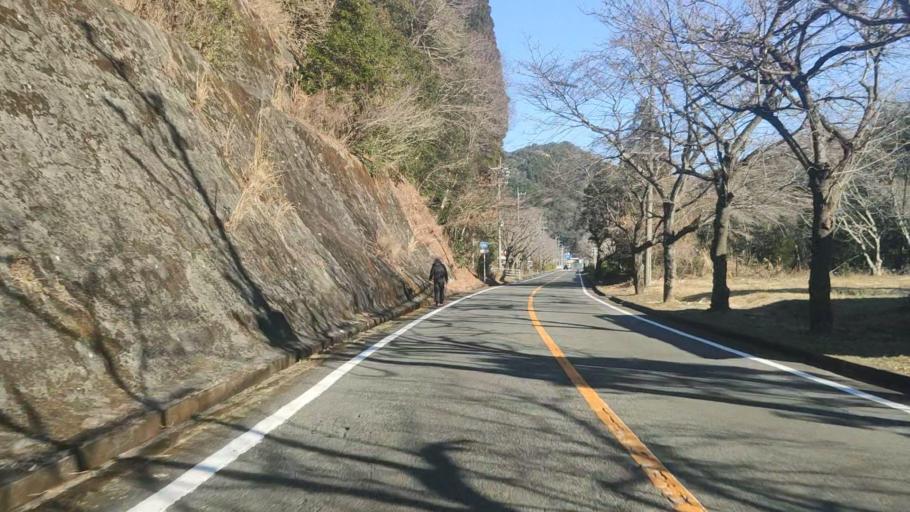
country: JP
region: Miyazaki
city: Nobeoka
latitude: 32.6414
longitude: 131.7445
